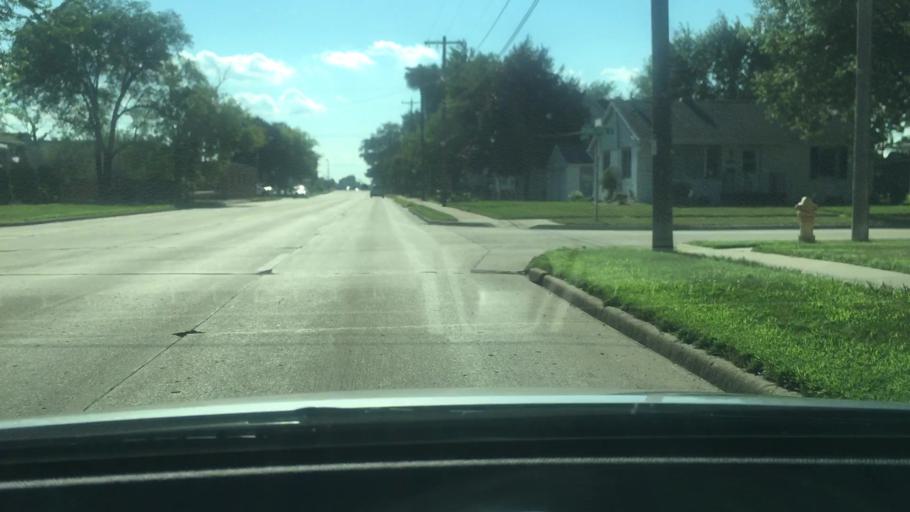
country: US
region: Wisconsin
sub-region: Winnebago County
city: Oshkosh
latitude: 43.9959
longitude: -88.5449
